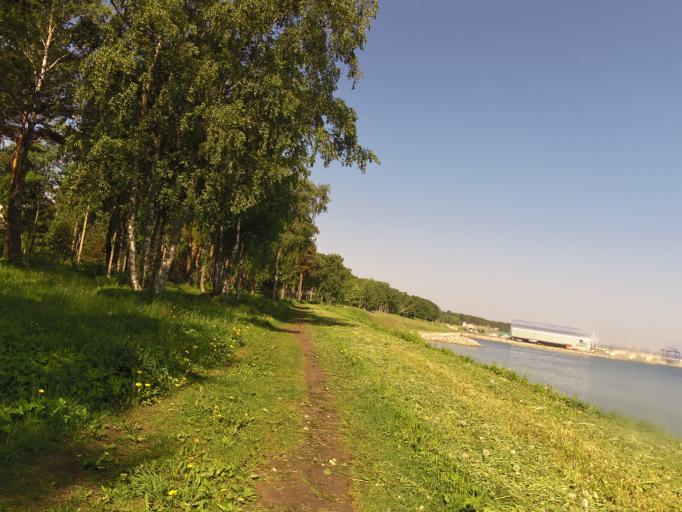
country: EE
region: Harju
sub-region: Harku vald
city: Tabasalu
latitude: 59.4475
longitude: 24.6111
